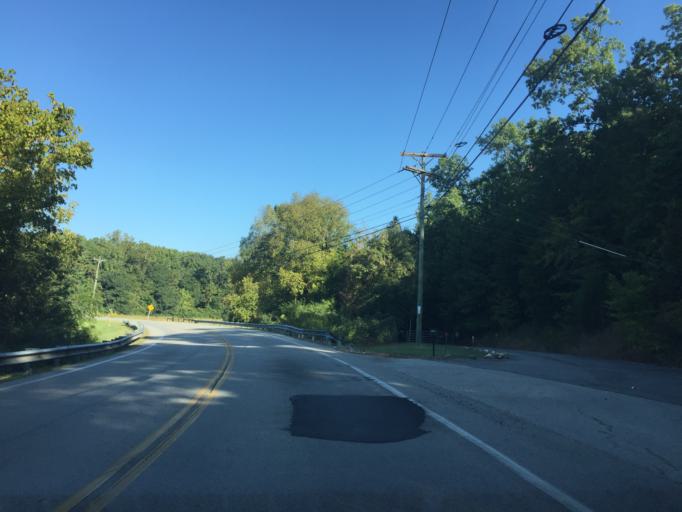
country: US
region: Tennessee
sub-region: Hamilton County
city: Harrison
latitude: 35.1195
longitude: -85.0837
